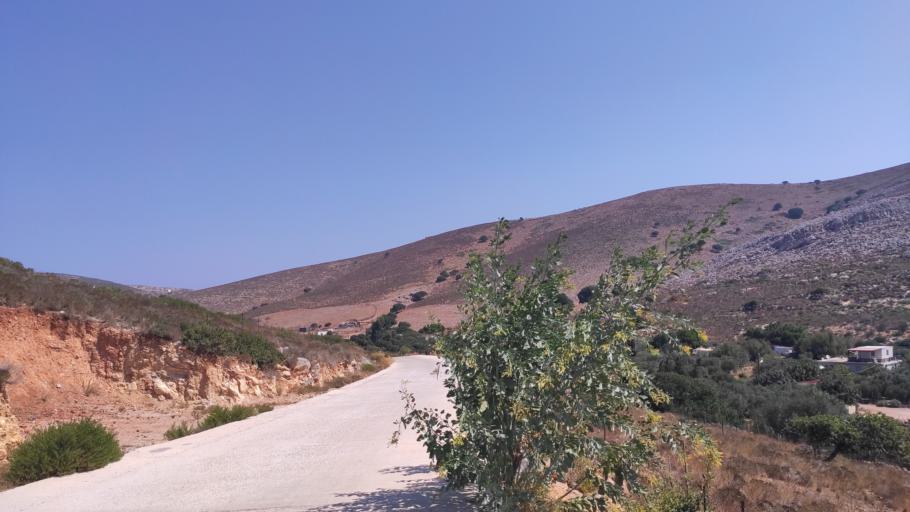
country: GR
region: South Aegean
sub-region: Nomos Dodekanisou
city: Pylion
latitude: 36.9357
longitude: 27.1342
